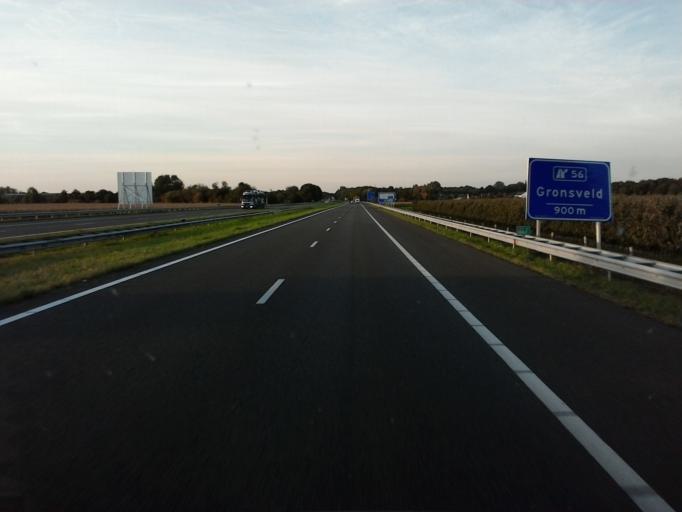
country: NL
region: Limburg
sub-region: Eijsden-Margraten
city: Eijsden
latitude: 50.8004
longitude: 5.7248
